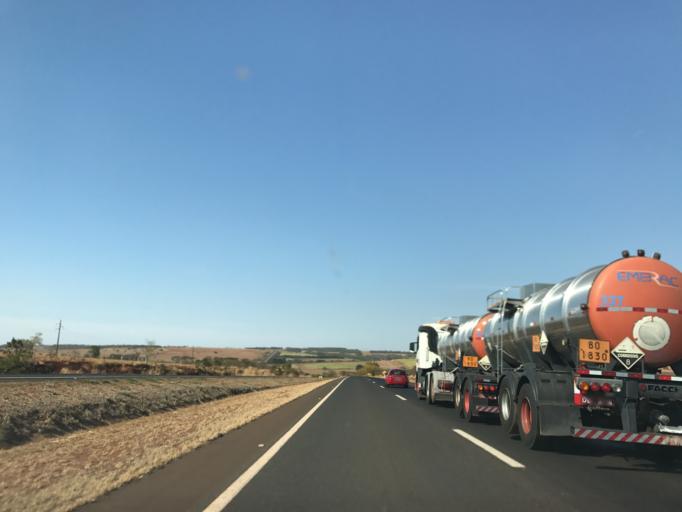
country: BR
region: Goias
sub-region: Goiatuba
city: Goiatuba
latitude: -17.9962
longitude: -49.2612
